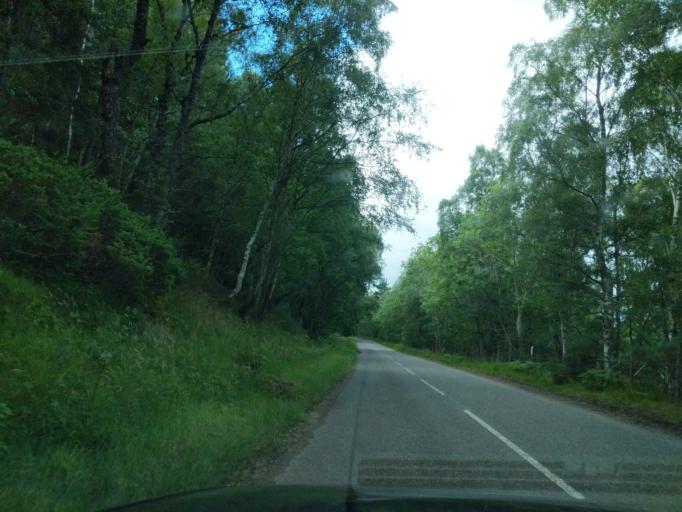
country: GB
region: Scotland
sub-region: Aberdeenshire
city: Aboyne
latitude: 57.0669
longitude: -2.9088
